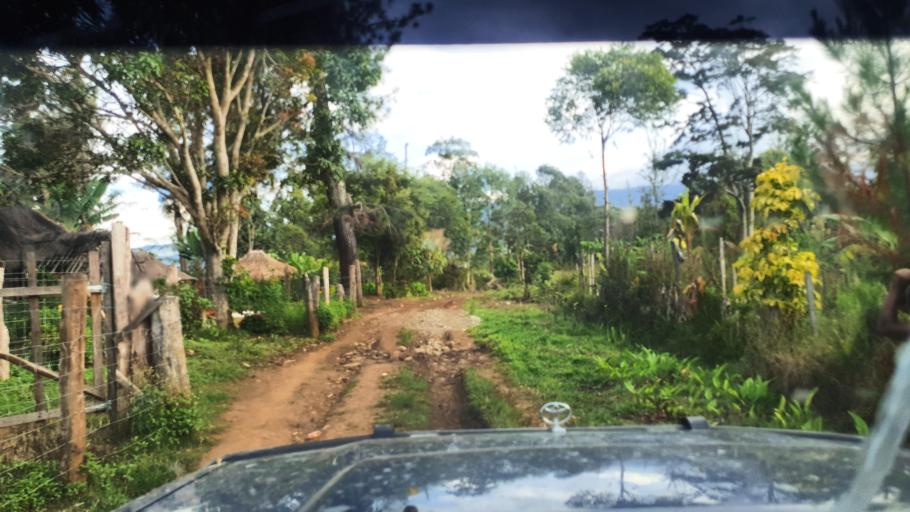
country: PG
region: Jiwaka
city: Minj
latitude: -5.9381
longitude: 144.8196
